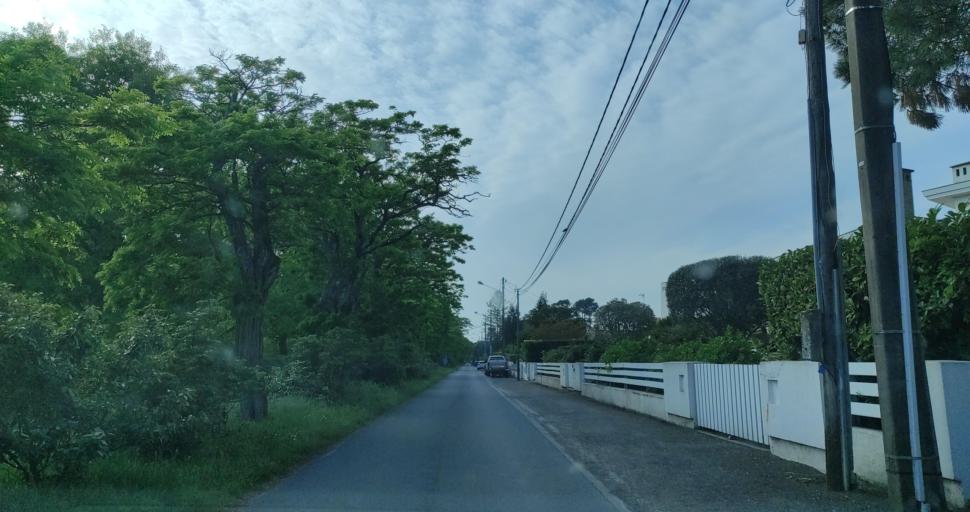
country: FR
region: Aquitaine
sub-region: Departement de la Gironde
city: Ares
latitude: 44.7538
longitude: -1.1282
